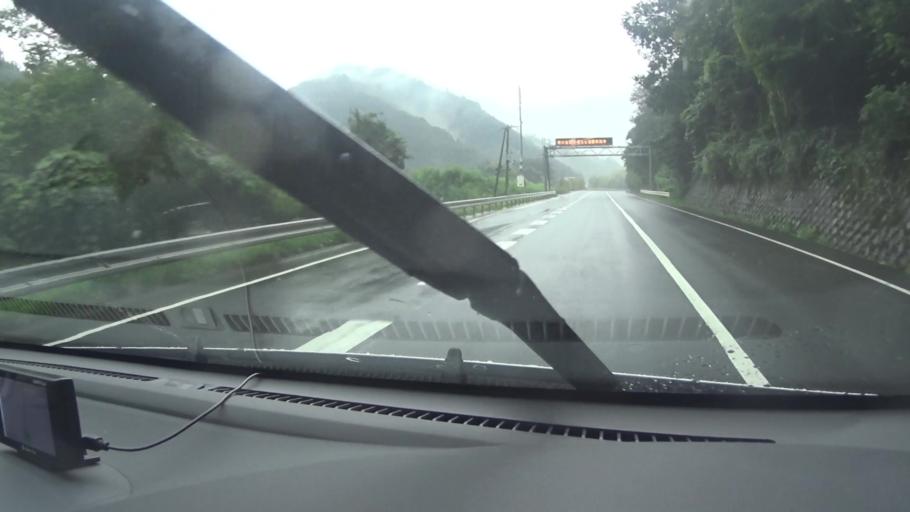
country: JP
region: Kyoto
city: Ayabe
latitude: 35.2869
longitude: 135.2664
